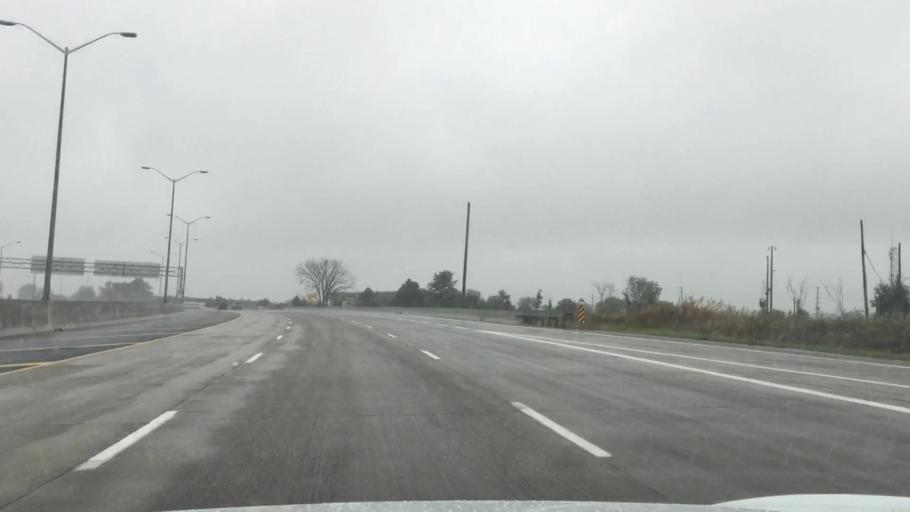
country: CA
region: Ontario
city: Windsor
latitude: 42.2333
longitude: -82.9880
